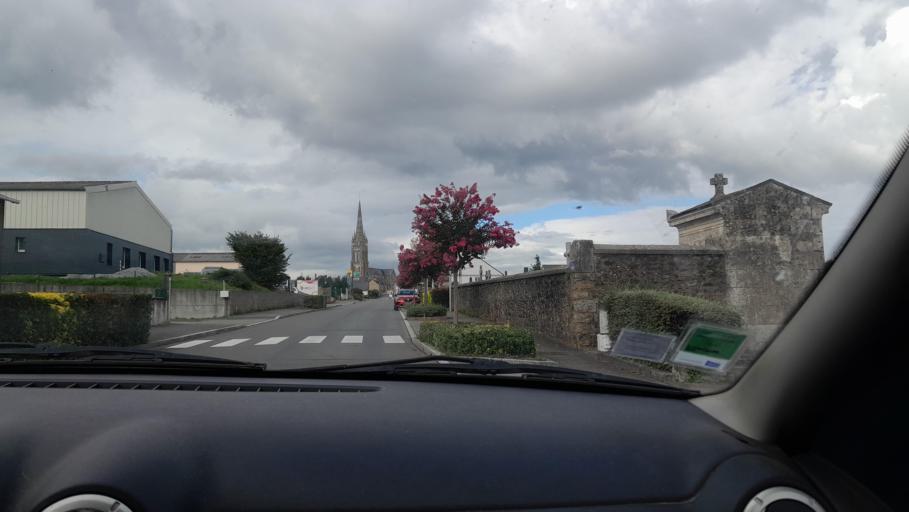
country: FR
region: Brittany
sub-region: Departement d'Ille-et-Vilaine
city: Le Pertre
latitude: 48.0298
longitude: -1.0366
